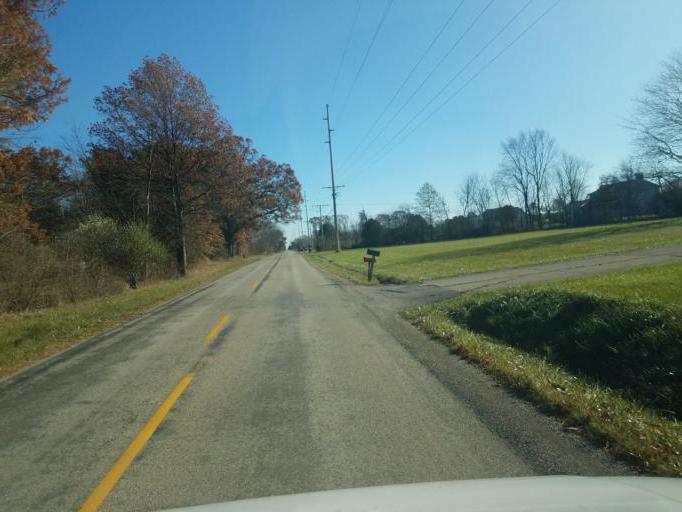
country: US
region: Ohio
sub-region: Ashland County
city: Ashland
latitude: 40.8290
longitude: -82.3442
